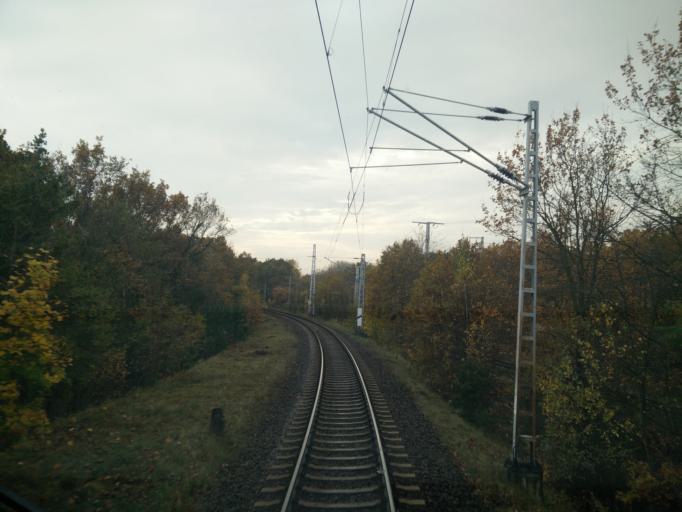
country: DE
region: Berlin
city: Adlershof
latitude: 52.4223
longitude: 13.5573
